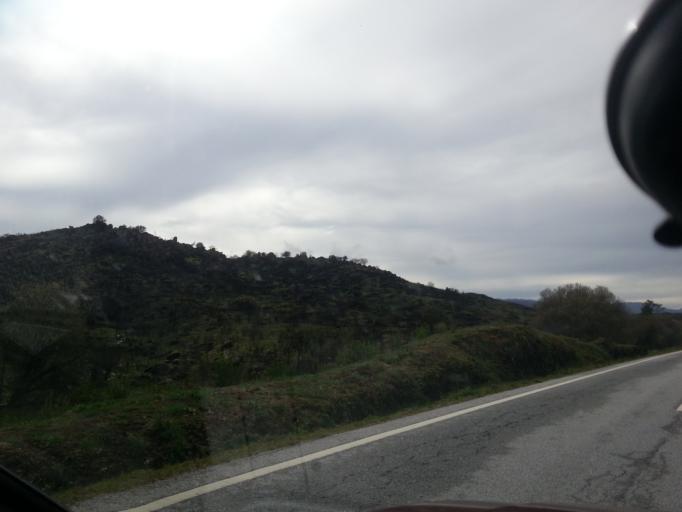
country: PT
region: Guarda
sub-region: Fornos de Algodres
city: Fornos de Algodres
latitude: 40.5636
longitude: -7.5583
